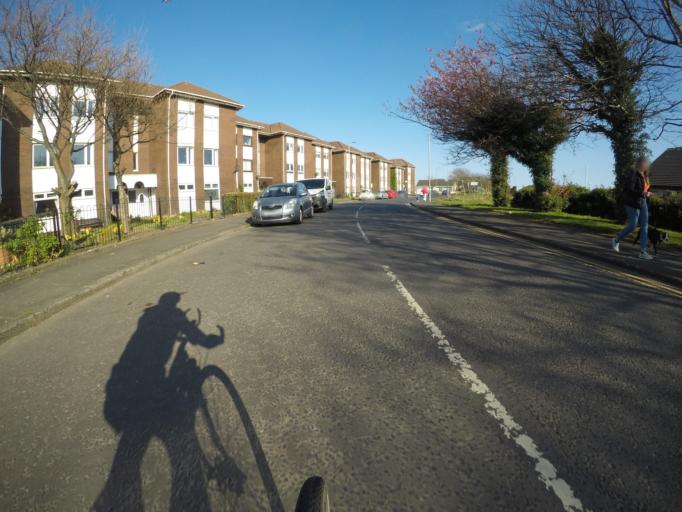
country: GB
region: Scotland
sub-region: North Ayrshire
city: Saltcoats
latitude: 55.6351
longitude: -4.7833
